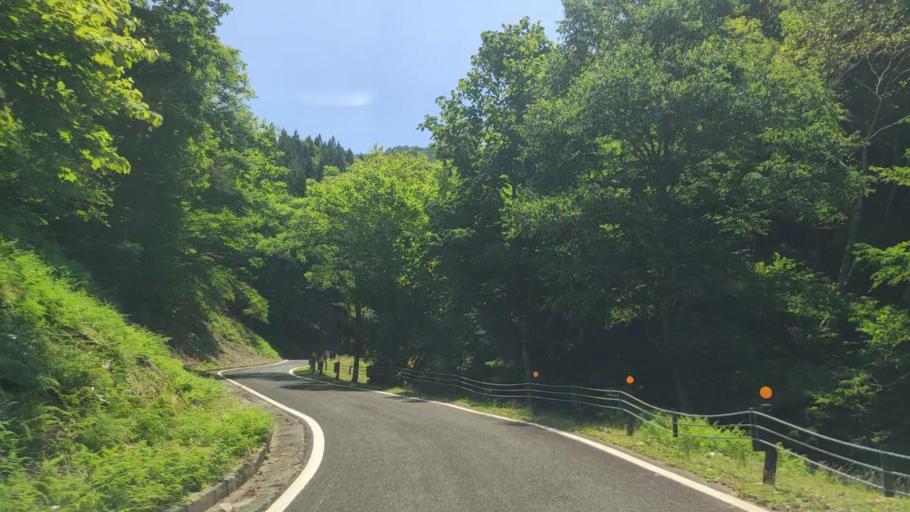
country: JP
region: Tottori
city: Tottori
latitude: 35.3732
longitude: 134.4914
